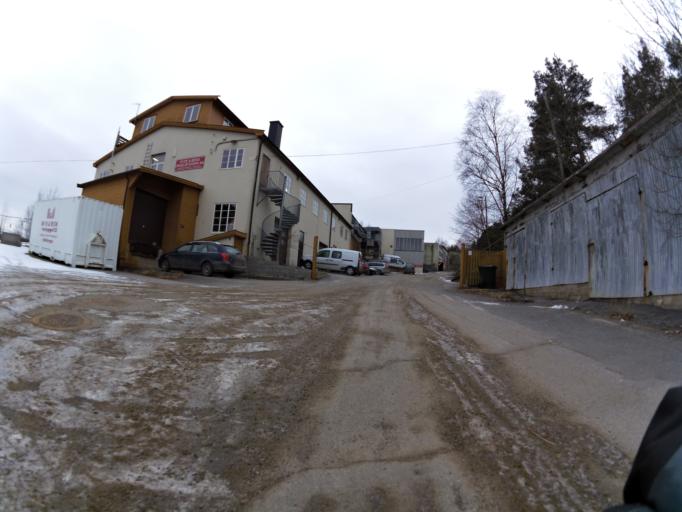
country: NO
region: Ostfold
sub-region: Fredrikstad
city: Fredrikstad
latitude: 59.2005
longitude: 10.8951
